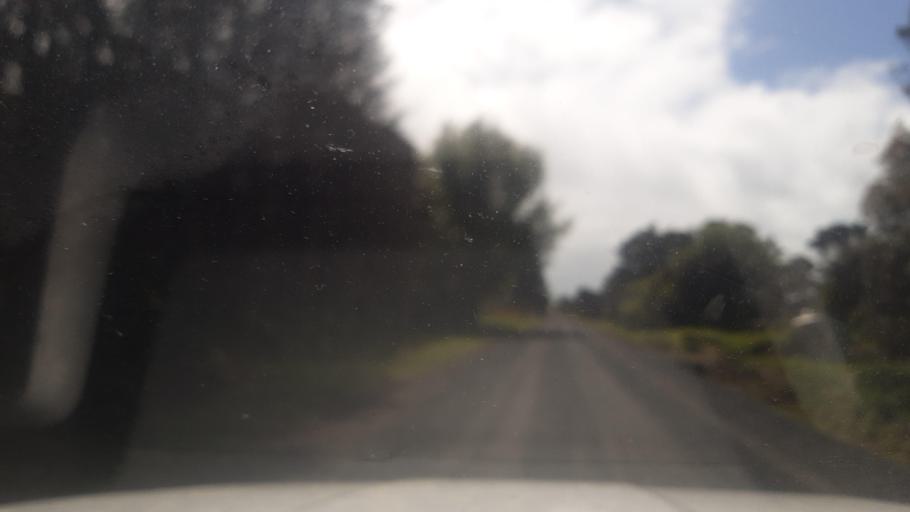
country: NZ
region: Northland
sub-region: Far North District
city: Kaitaia
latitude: -34.7430
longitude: 173.1073
